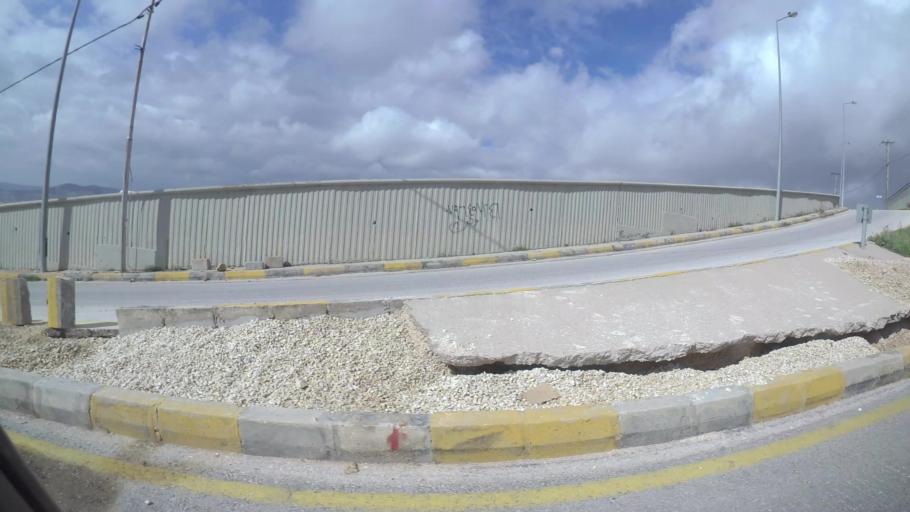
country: JO
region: Amman
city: Al Jubayhah
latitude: 32.0712
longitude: 35.8759
